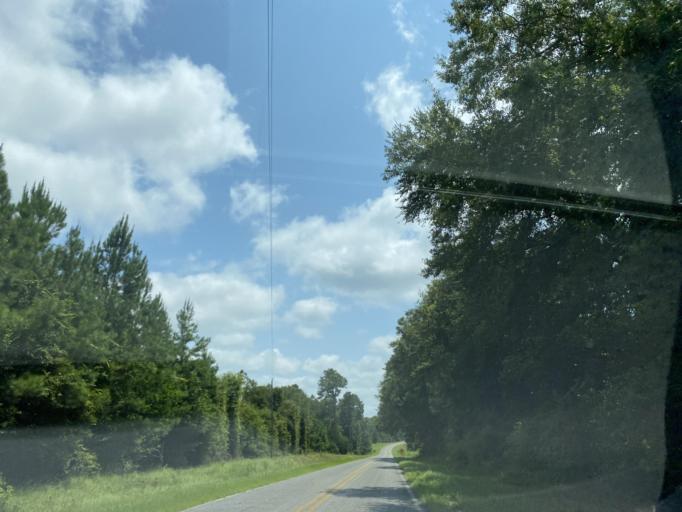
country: US
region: Georgia
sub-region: Wheeler County
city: Alamo
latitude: 32.0763
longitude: -82.7370
